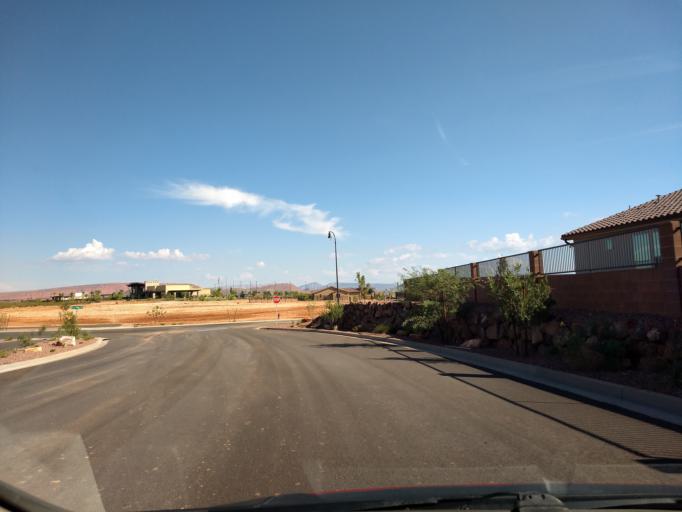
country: US
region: Utah
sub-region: Washington County
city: Washington
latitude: 37.1450
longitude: -113.5155
